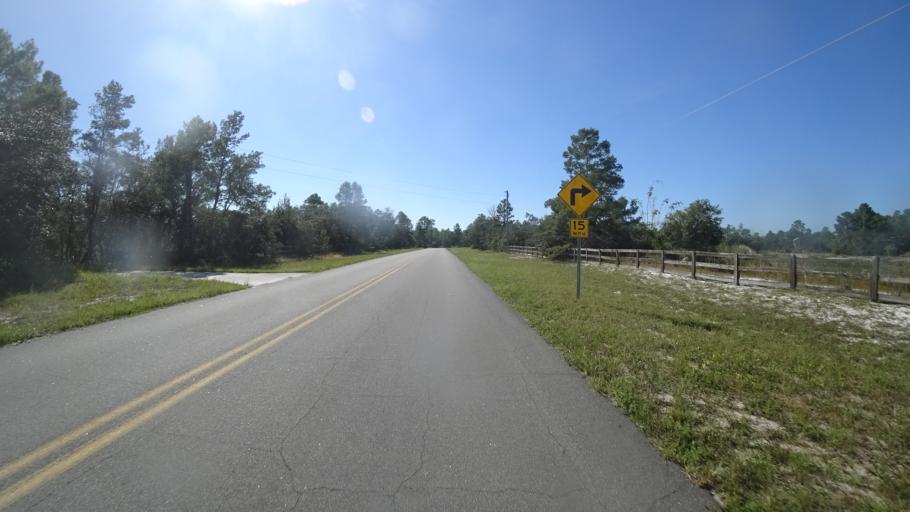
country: US
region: Florida
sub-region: Sarasota County
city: Lake Sarasota
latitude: 27.3574
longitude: -82.2375
